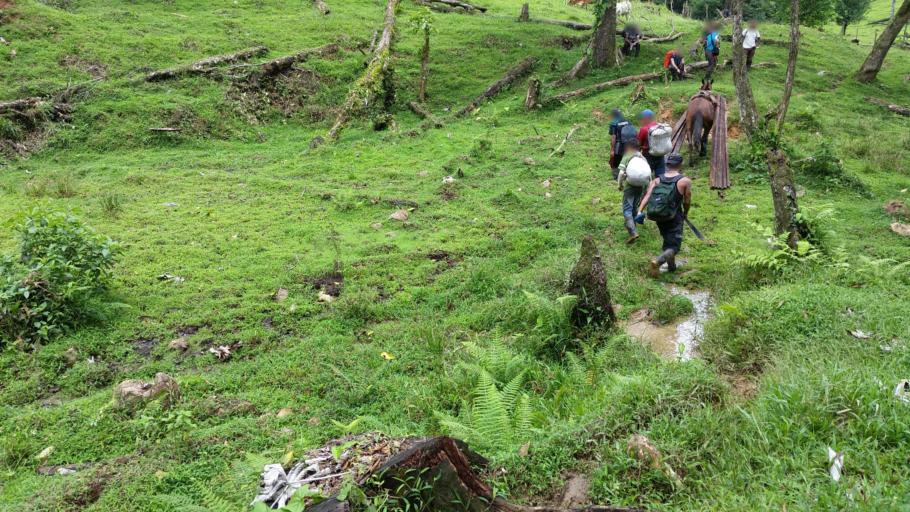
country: NI
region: Atlantico Norte (RAAN)
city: Bonanza
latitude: 13.9922
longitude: -84.7539
